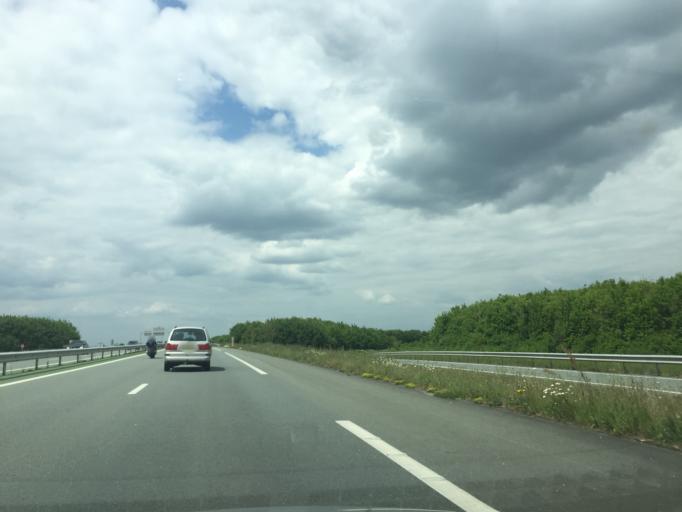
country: FR
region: Poitou-Charentes
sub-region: Departement des Deux-Sevres
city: Saint-Gelais
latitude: 46.4137
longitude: -0.3958
